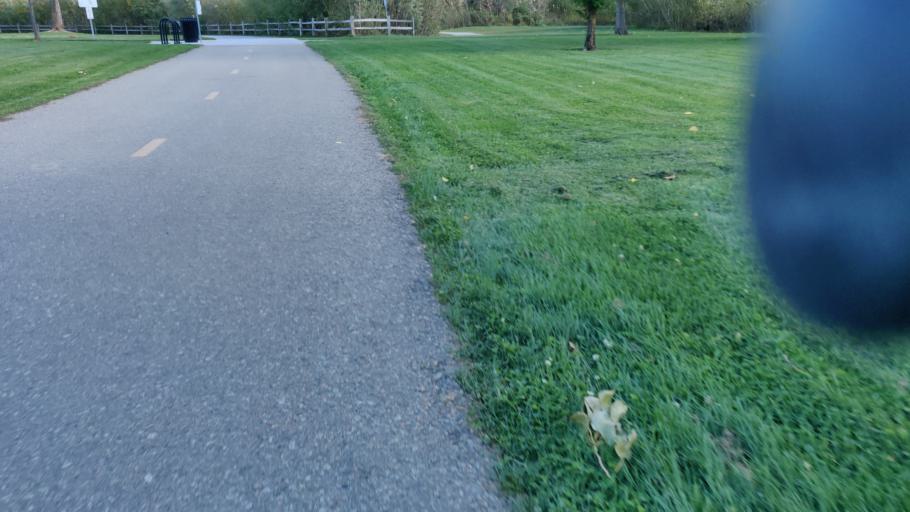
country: US
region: Idaho
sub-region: Ada County
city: Boise
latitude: 43.5719
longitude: -116.1441
